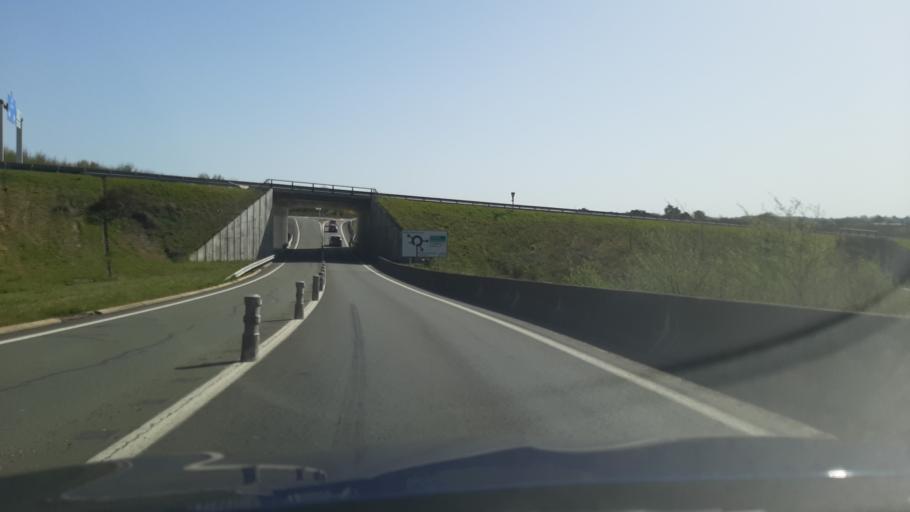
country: FR
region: Pays de la Loire
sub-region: Departement de Maine-et-Loire
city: Murs-Erigne
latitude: 47.3924
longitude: -0.5439
